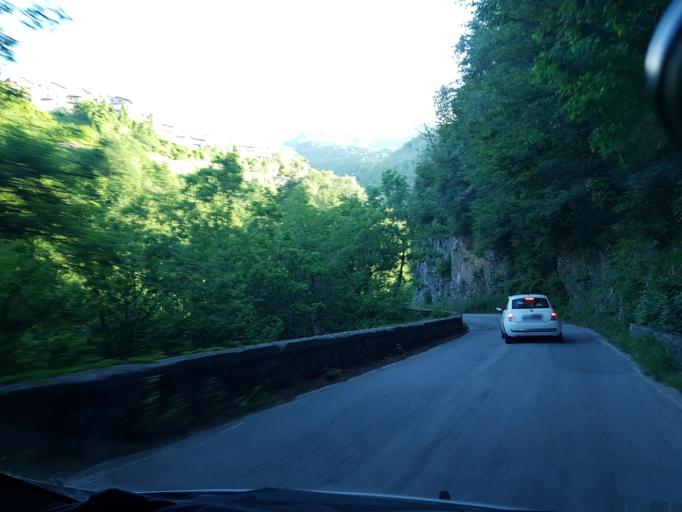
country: IT
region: Tuscany
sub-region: Provincia di Lucca
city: Minucciano
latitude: 44.1728
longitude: 10.2069
